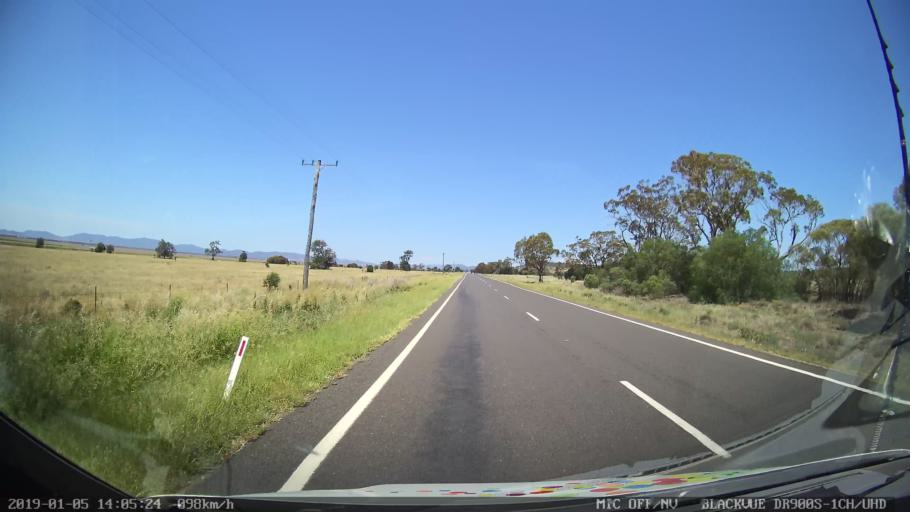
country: AU
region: New South Wales
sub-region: Gunnedah
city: Gunnedah
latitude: -31.2104
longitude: 150.3751
